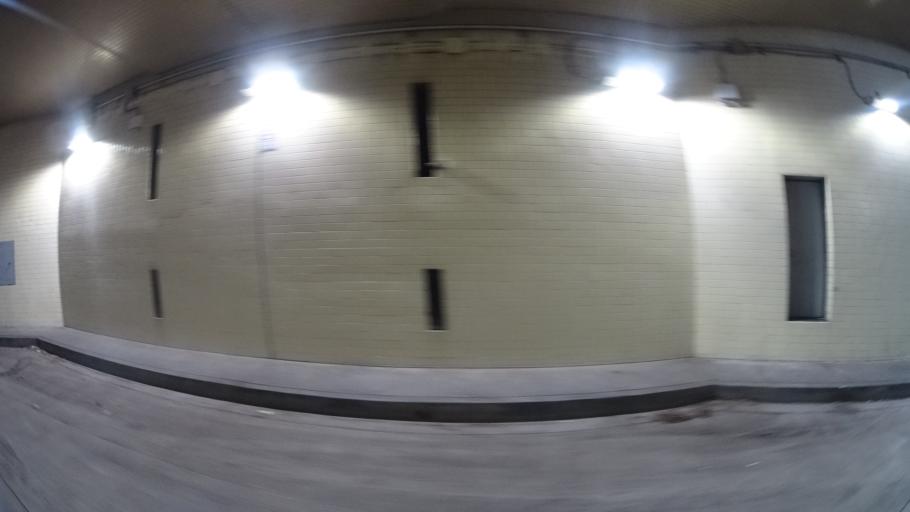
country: US
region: California
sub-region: Los Angeles County
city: Van Nuys
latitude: 34.2011
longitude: -118.4894
